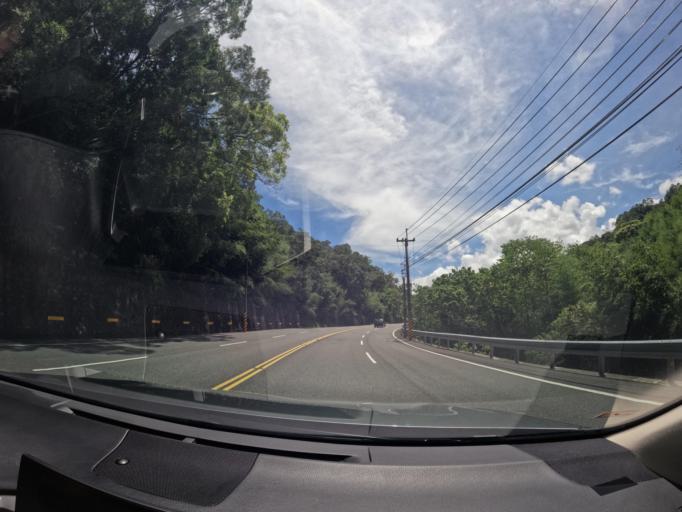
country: TW
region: Taiwan
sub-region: Miaoli
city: Miaoli
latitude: 24.5045
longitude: 120.9061
